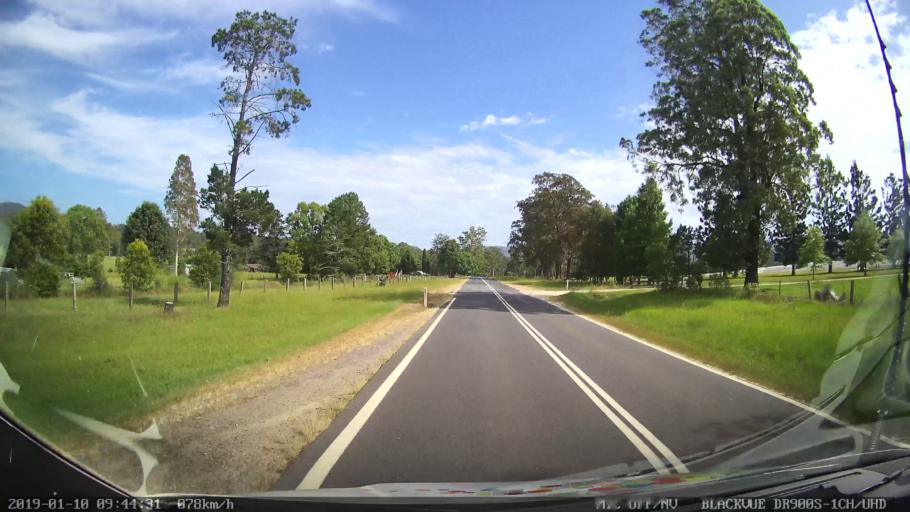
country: AU
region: New South Wales
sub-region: Coffs Harbour
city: Nana Glen
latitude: -30.1158
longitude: 153.0036
